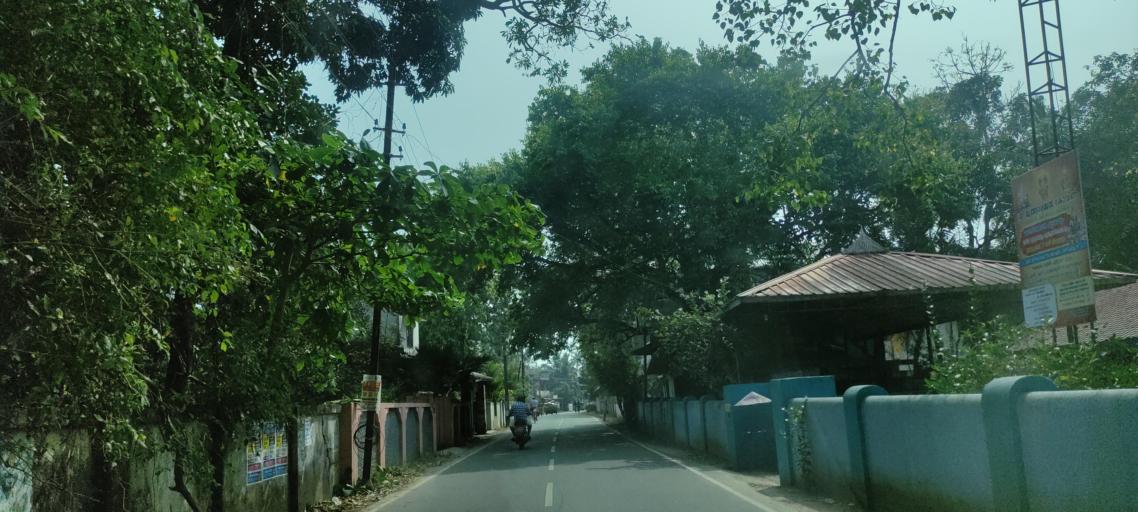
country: IN
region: Kerala
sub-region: Alappuzha
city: Vayalar
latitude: 9.6866
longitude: 76.3340
